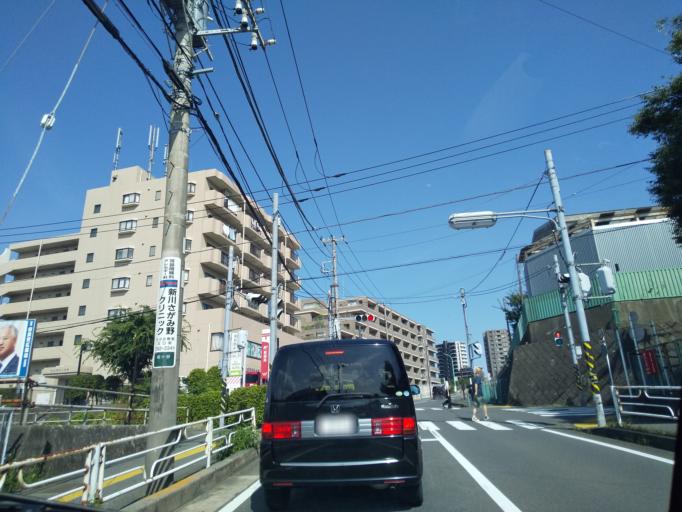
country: JP
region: Kanagawa
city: Zama
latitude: 35.4684
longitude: 139.4127
